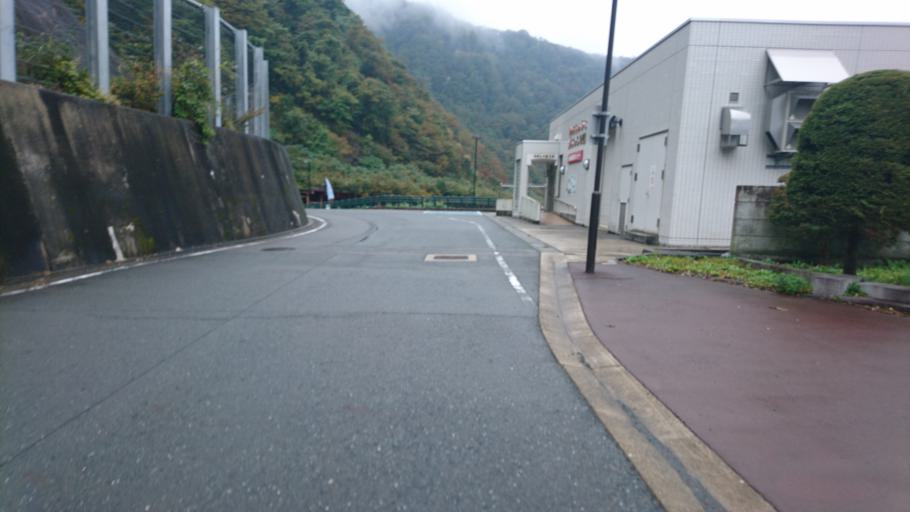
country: JP
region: Iwate
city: Kitakami
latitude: 39.3026
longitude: 140.8834
